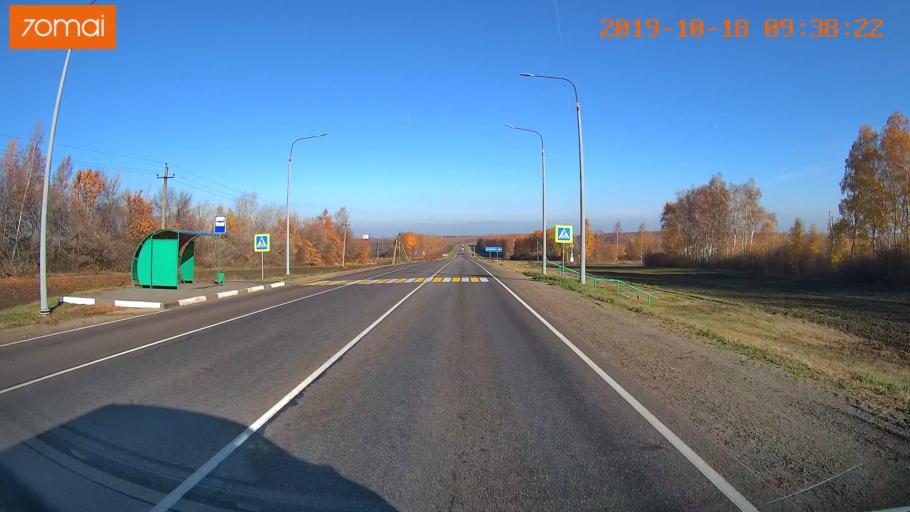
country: RU
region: Tula
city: Yefremov
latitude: 53.2369
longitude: 38.1374
